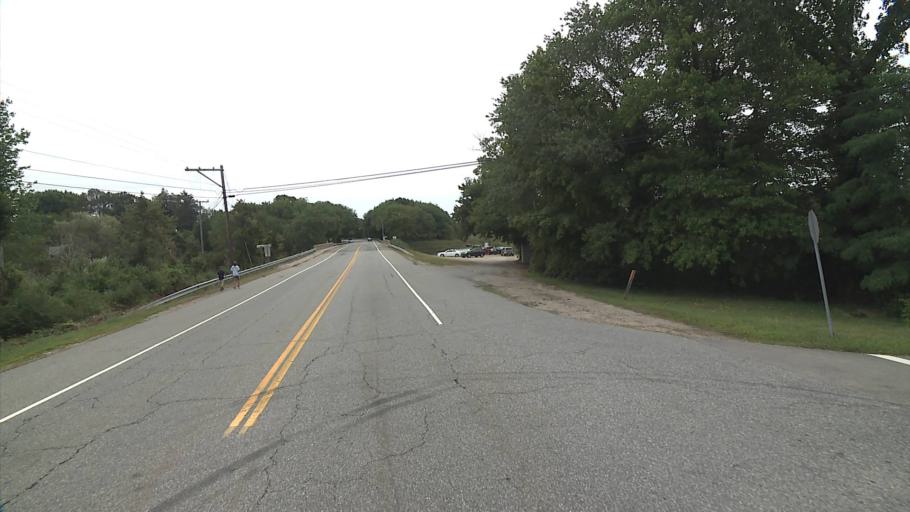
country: US
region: Connecticut
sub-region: Middlesex County
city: Old Saybrook Center
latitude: 41.3150
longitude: -72.3374
